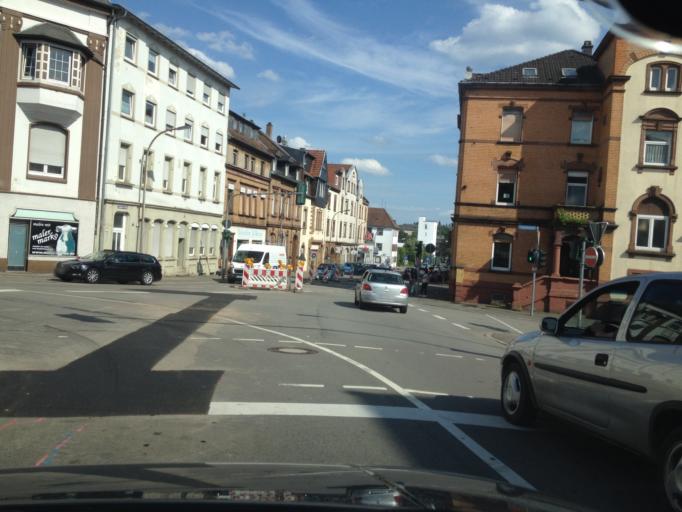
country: DE
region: Rheinland-Pfalz
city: Pirmasens
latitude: 49.1931
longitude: 7.6124
